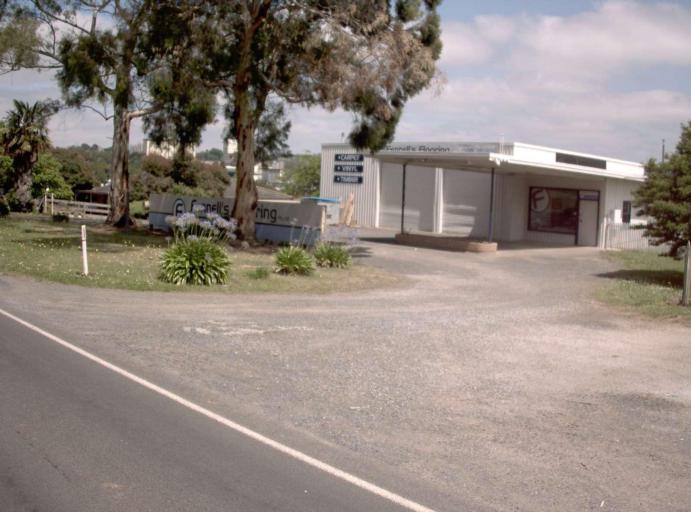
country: AU
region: Victoria
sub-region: Baw Baw
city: Warragul
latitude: -38.4659
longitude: 145.9637
